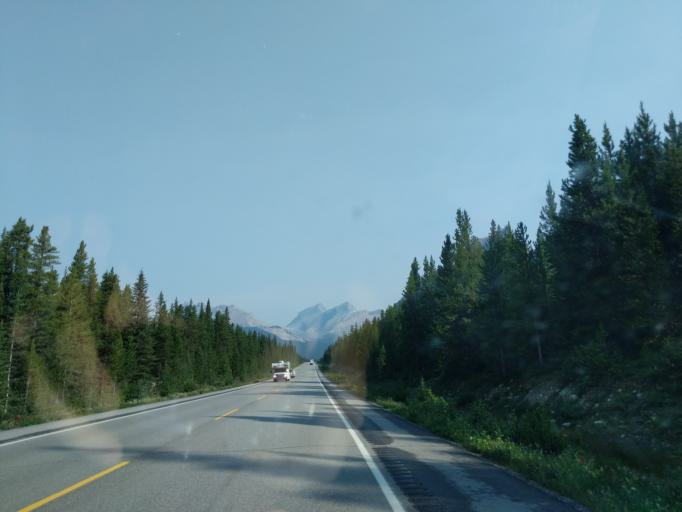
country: CA
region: Alberta
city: Lake Louise
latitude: 51.6040
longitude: -116.3105
